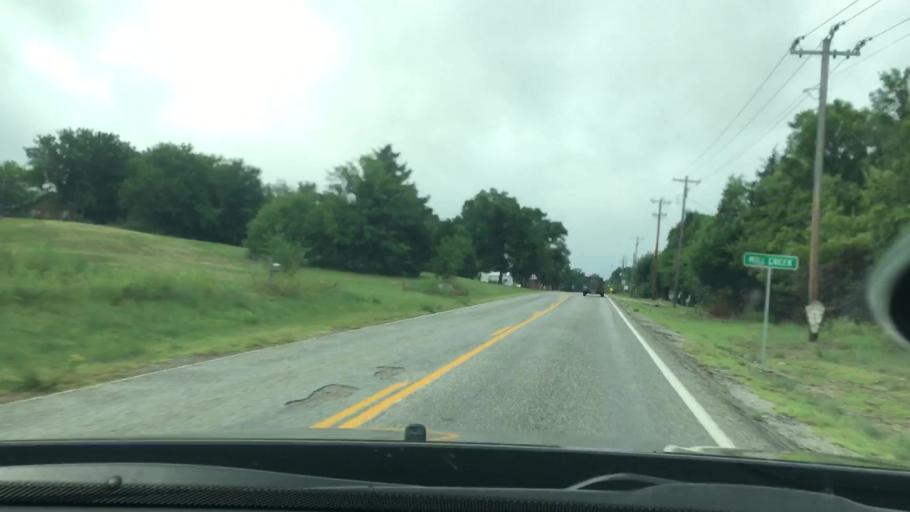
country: US
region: Oklahoma
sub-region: Murray County
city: Sulphur
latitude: 34.4069
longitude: -96.8271
